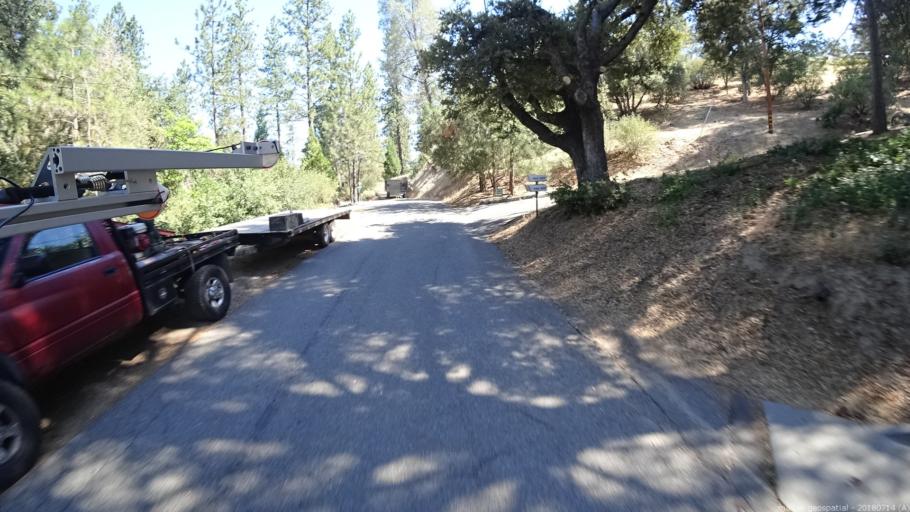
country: US
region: California
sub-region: Madera County
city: Oakhurst
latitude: 37.3734
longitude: -119.6226
